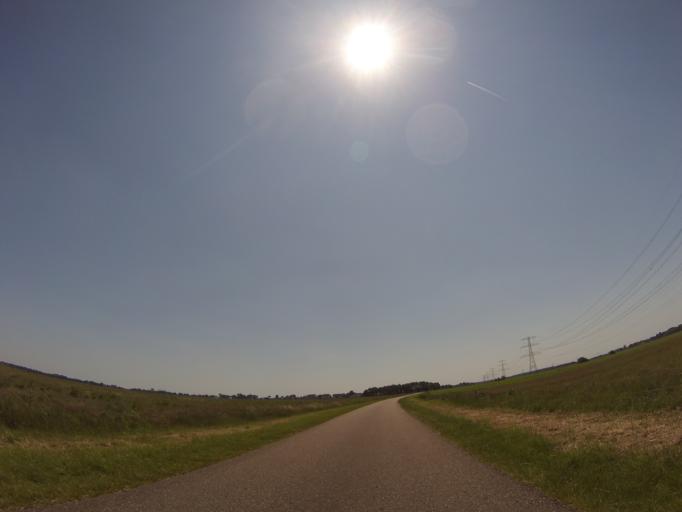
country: NL
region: Drenthe
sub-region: Gemeente Coevorden
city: Sleen
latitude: 52.7538
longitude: 6.8431
